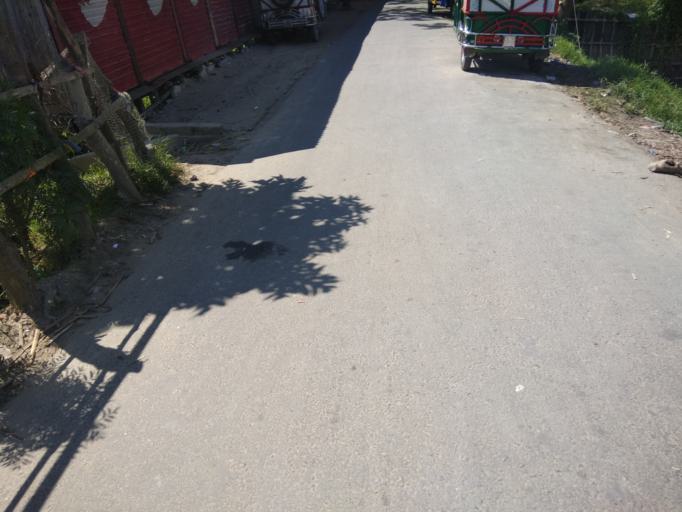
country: BD
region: Dhaka
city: Narayanganj
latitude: 23.4411
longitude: 90.4799
